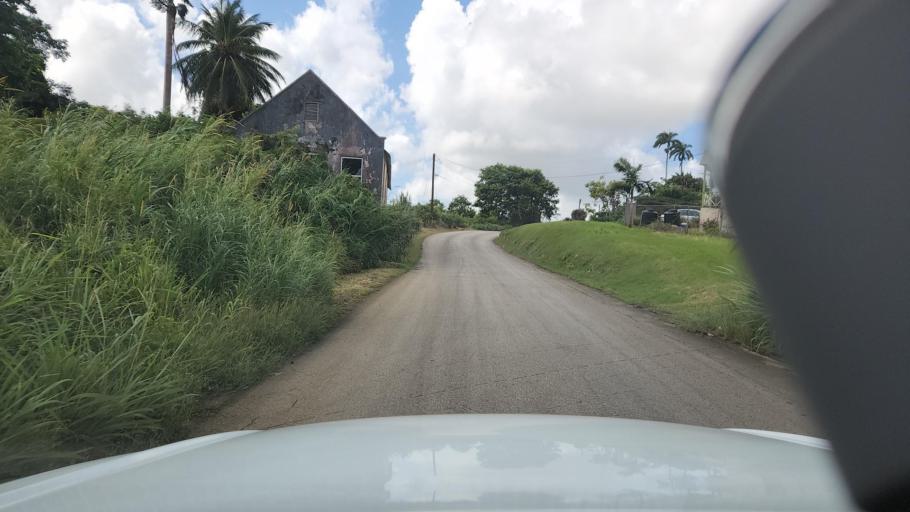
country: BB
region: Saint Joseph
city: Bathsheba
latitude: 13.1941
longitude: -59.5242
